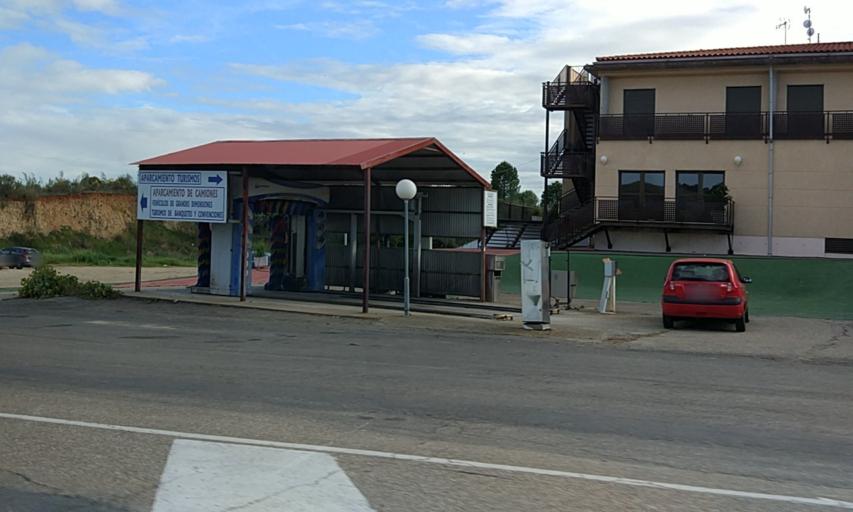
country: ES
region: Extremadura
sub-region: Provincia de Caceres
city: Coria
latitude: 40.0050
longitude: -6.5543
